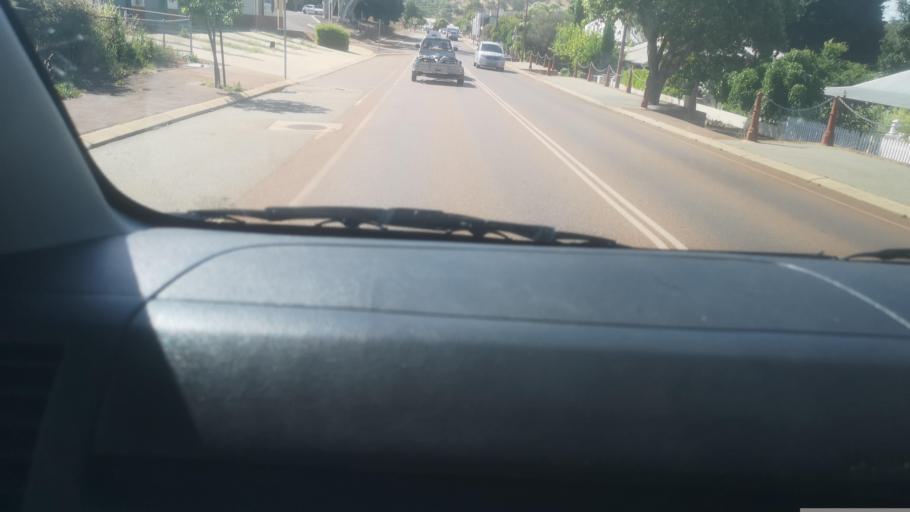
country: AU
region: Western Australia
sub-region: Toodyay
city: Toodyay
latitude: -31.5529
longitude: 116.4722
